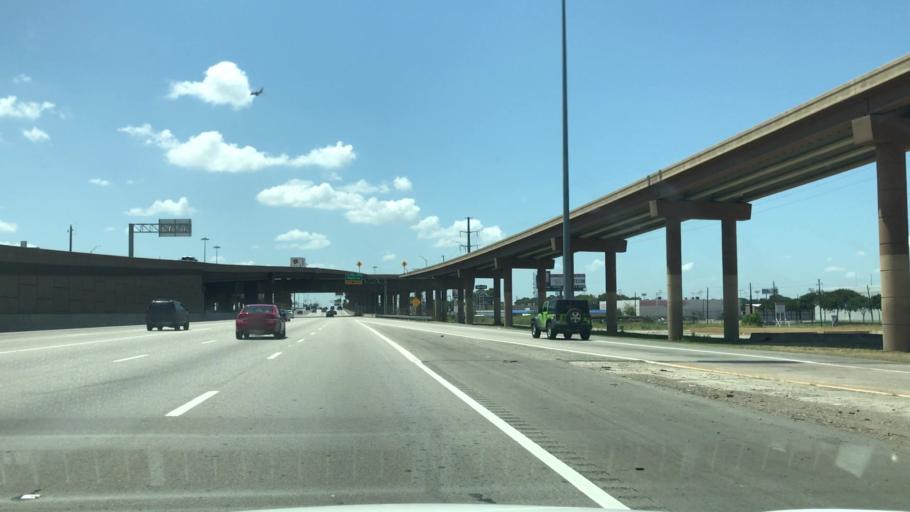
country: US
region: Texas
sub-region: Dallas County
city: Farmers Branch
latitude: 32.9047
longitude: -96.8982
